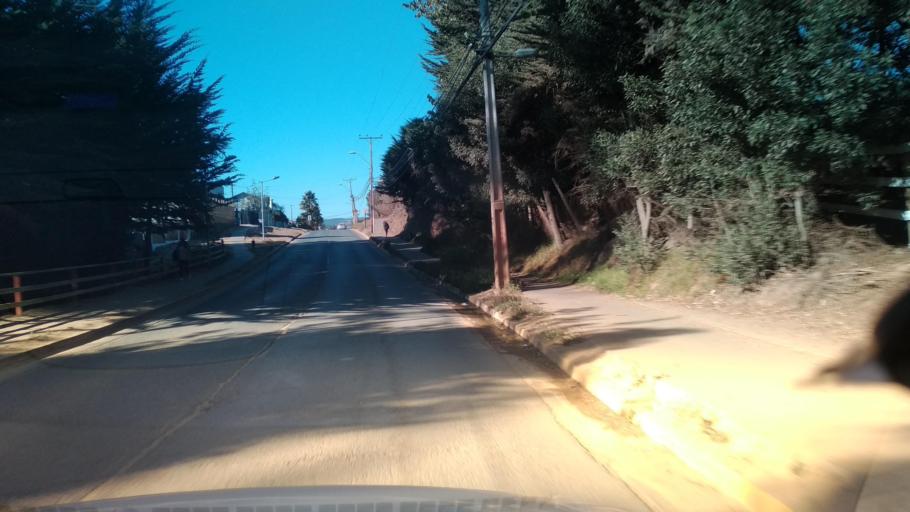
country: CL
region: O'Higgins
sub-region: Provincia de Colchagua
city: Santa Cruz
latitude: -34.3935
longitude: -72.0098
